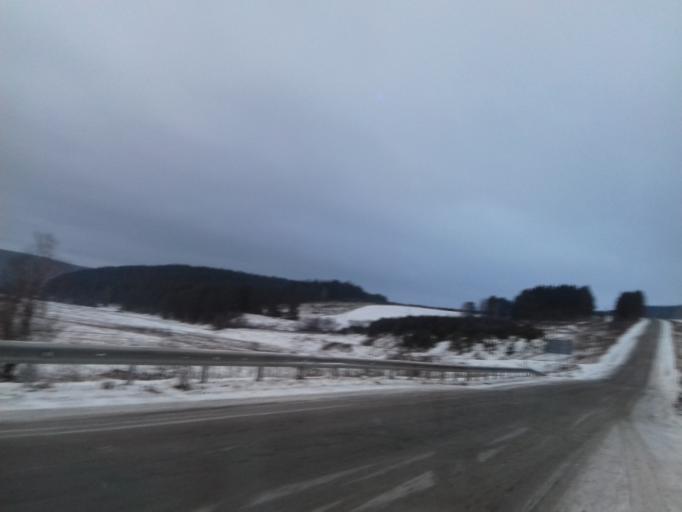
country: RU
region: Bashkortostan
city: Verkhniy Avzyan
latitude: 53.5046
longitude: 57.6769
